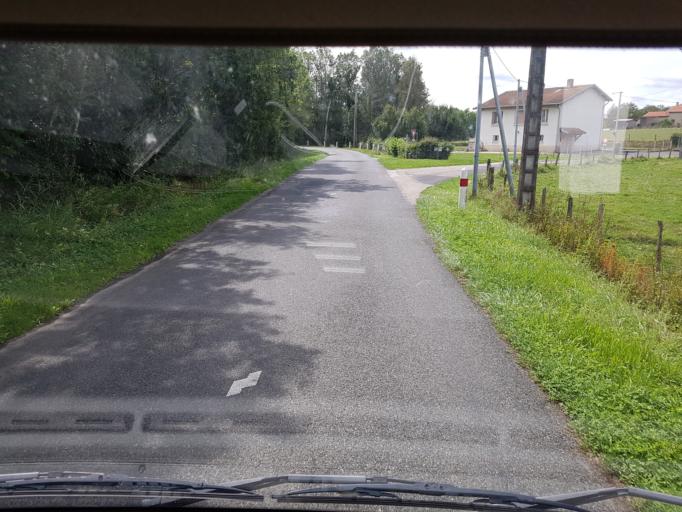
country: FR
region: Rhone-Alpes
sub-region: Departement de l'Ain
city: Villars-les-Dombes
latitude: 45.9520
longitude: 5.0837
